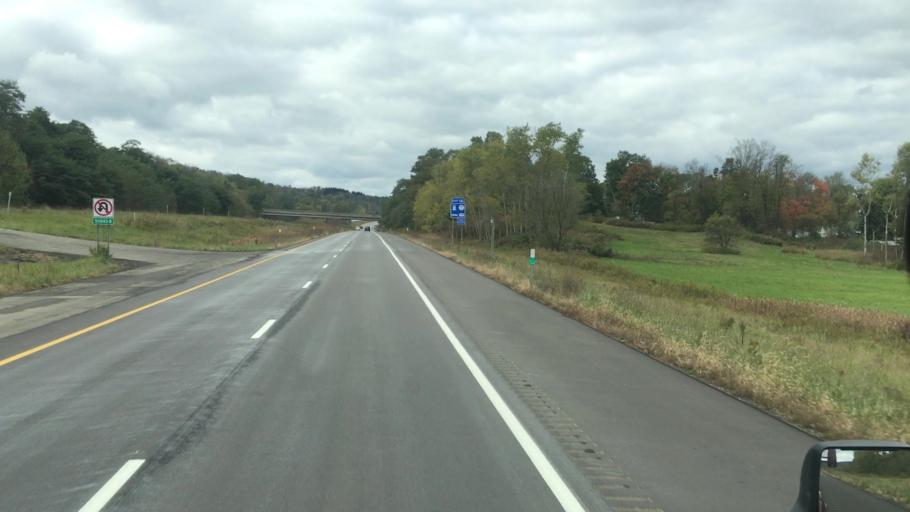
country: US
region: New York
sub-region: Cattaraugus County
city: Randolph
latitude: 42.1539
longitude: -78.9810
